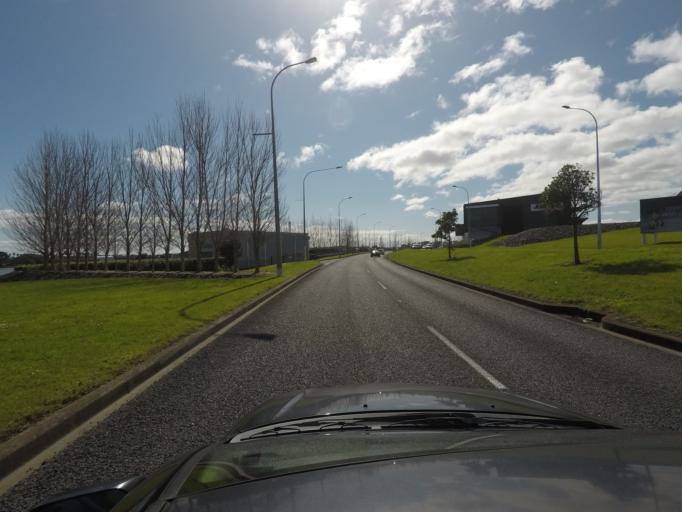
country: NZ
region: Auckland
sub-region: Auckland
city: Tamaki
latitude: -36.9413
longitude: 174.8632
